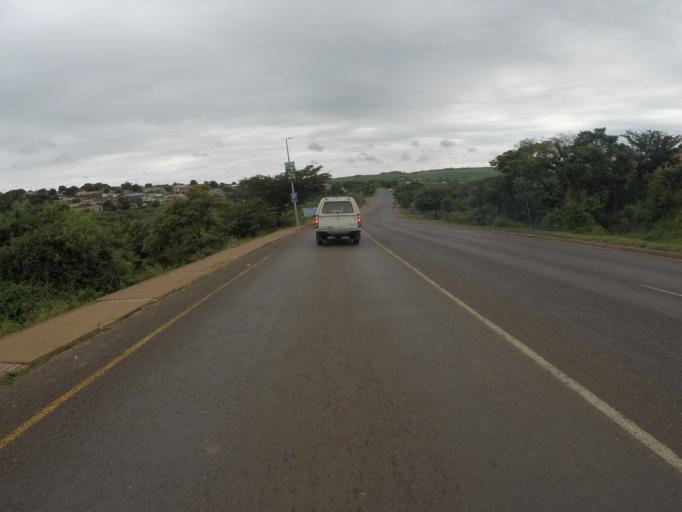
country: ZA
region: KwaZulu-Natal
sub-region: uThungulu District Municipality
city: Empangeni
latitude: -28.7754
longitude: 31.8742
